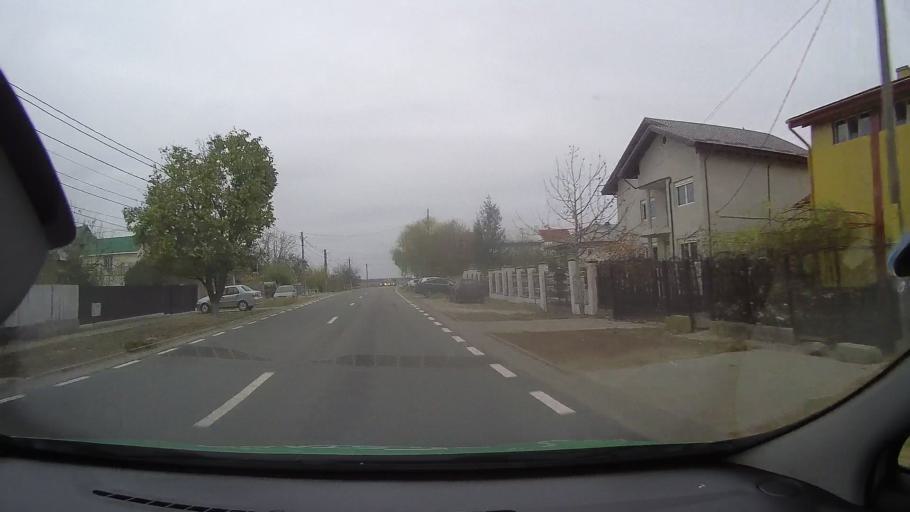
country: RO
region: Ialomita
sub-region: Comuna Slobozia
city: Slobozia
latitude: 44.5967
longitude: 27.3902
